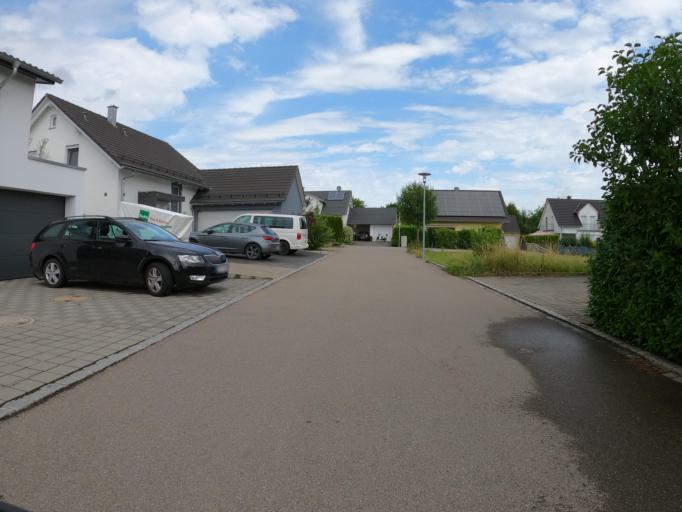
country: DE
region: Baden-Wuerttemberg
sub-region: Tuebingen Region
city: Langenau
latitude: 48.5075
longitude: 10.1288
